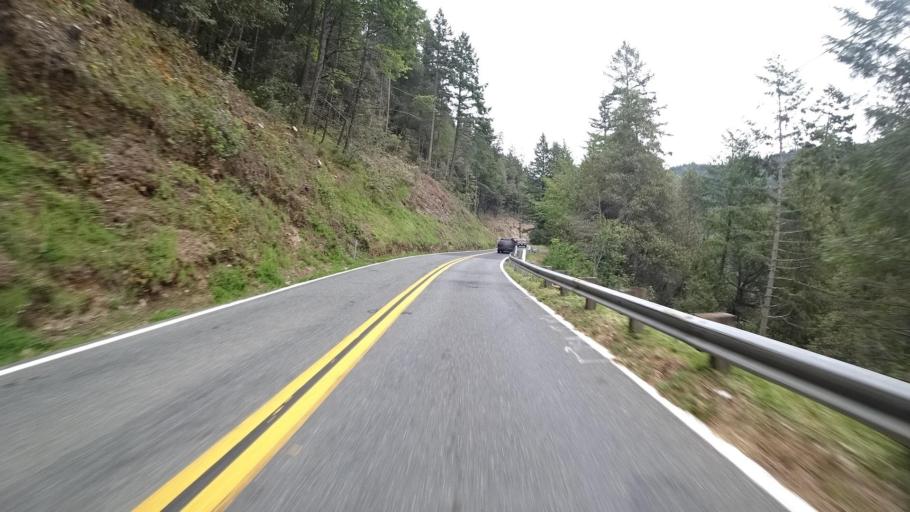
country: US
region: California
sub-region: Humboldt County
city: Willow Creek
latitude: 41.0139
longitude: -123.6371
